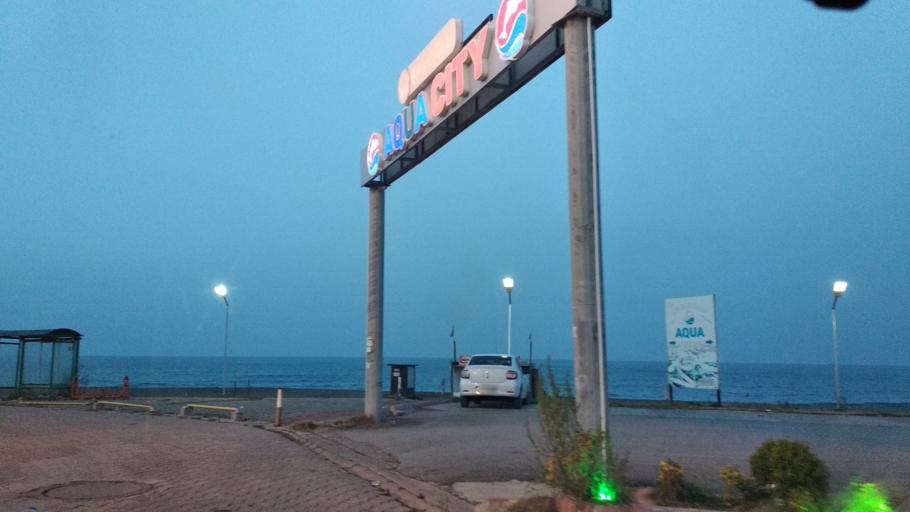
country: TR
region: Sakarya
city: Karasu
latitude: 41.0910
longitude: 30.7422
